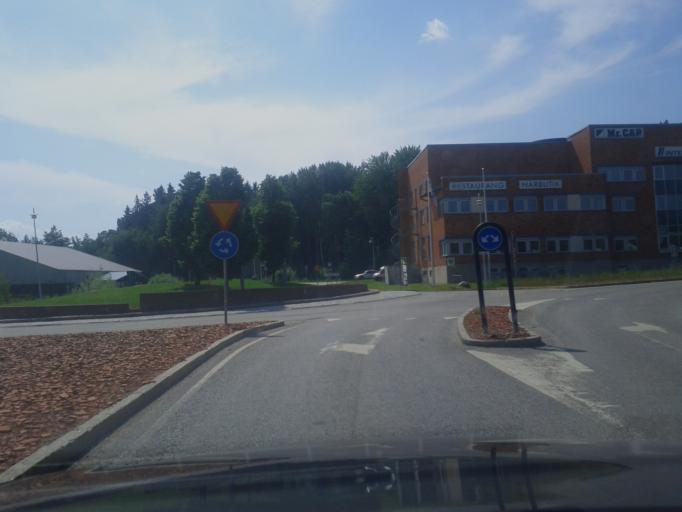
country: SE
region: Stockholm
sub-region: Taby Kommun
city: Taby
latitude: 59.4456
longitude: 18.1222
